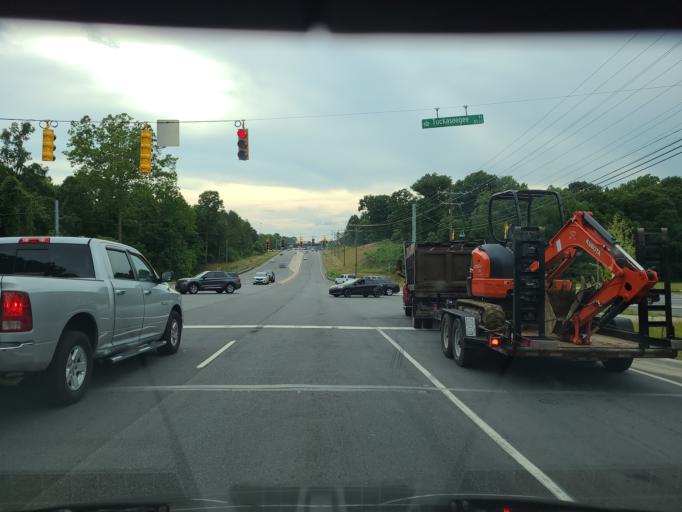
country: US
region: North Carolina
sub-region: Gaston County
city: Belmont
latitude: 35.2384
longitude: -80.9619
